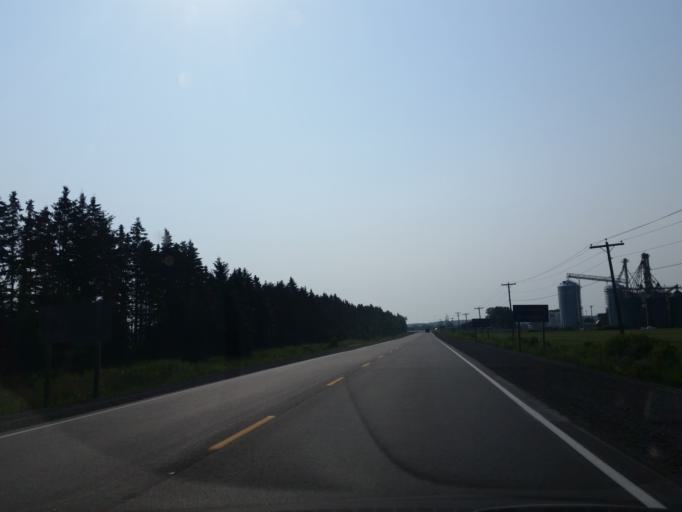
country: CA
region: Ontario
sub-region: Nipissing District
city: North Bay
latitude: 46.4095
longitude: -80.1088
